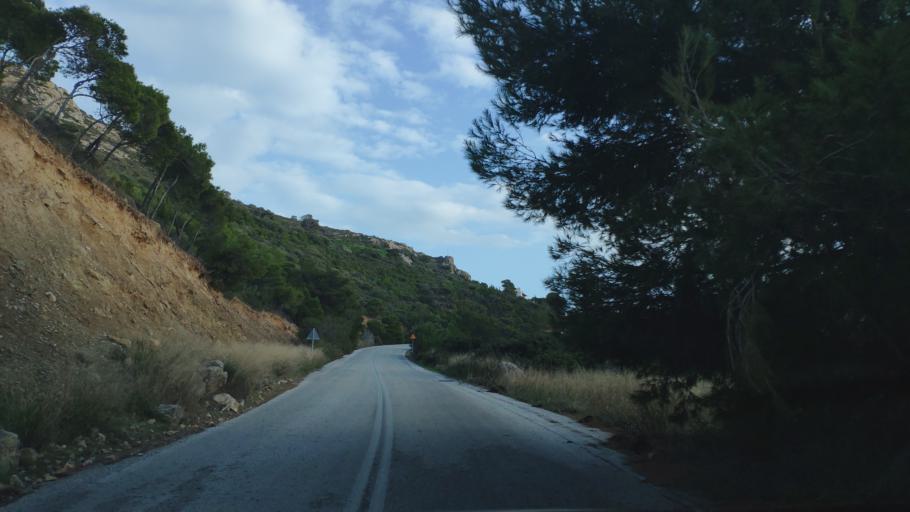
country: GR
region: Attica
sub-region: Nomarchia Anatolikis Attikis
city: Limin Mesoyaias
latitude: 37.9112
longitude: 24.0166
